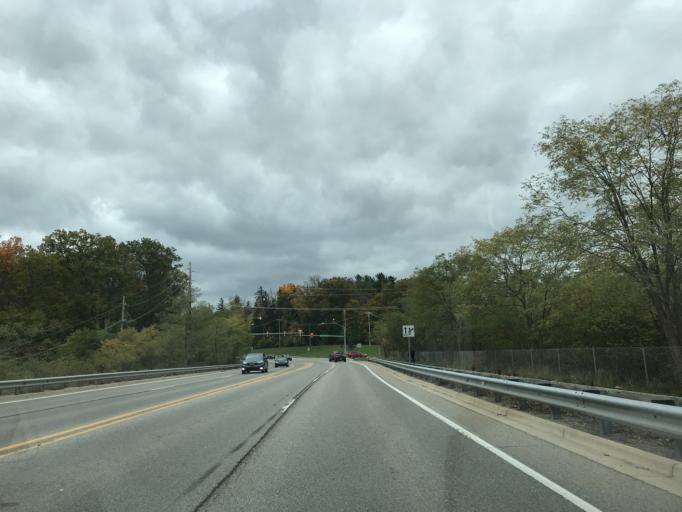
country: US
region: Michigan
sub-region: Washtenaw County
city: Ypsilanti
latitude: 42.2696
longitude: -83.6701
